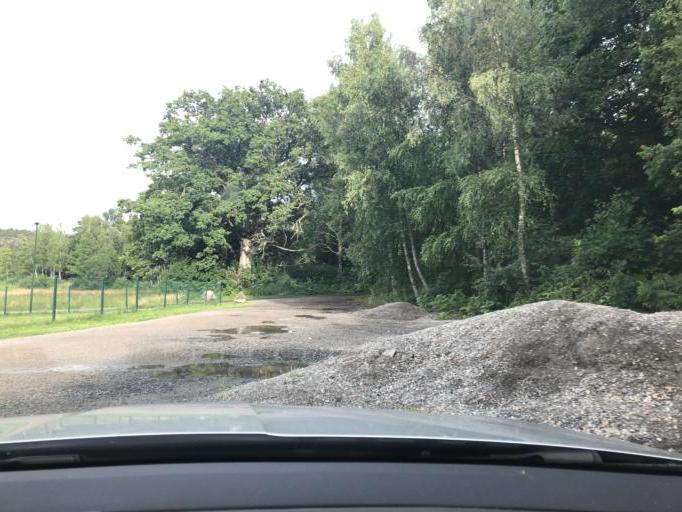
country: SE
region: Stockholm
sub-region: Botkyrka Kommun
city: Alby
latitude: 59.2318
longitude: 17.8654
